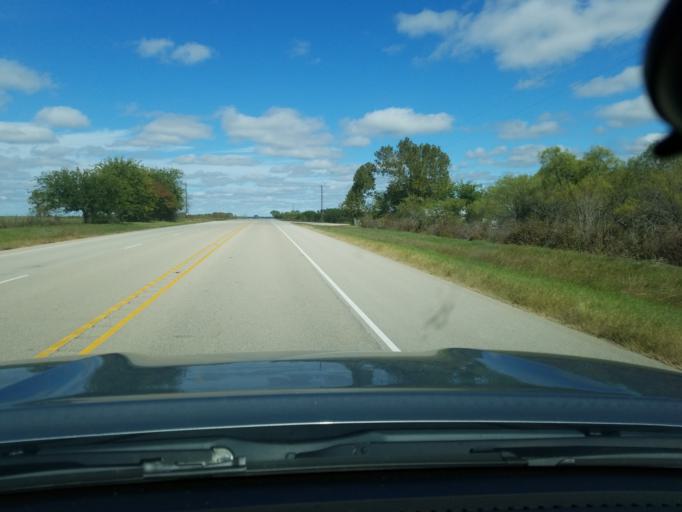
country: US
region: Texas
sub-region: Hamilton County
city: Hamilton
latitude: 31.5684
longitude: -98.1584
